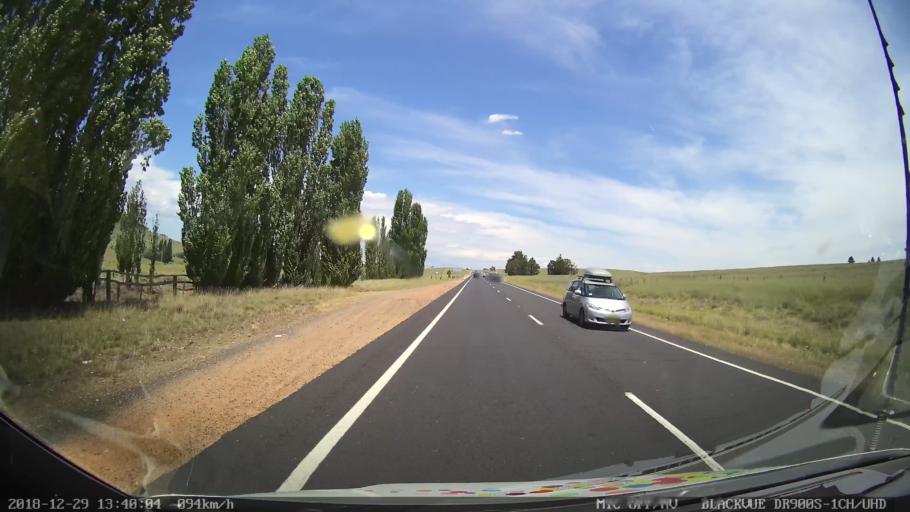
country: AU
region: New South Wales
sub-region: Cooma-Monaro
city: Cooma
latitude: -36.0219
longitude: 149.1502
